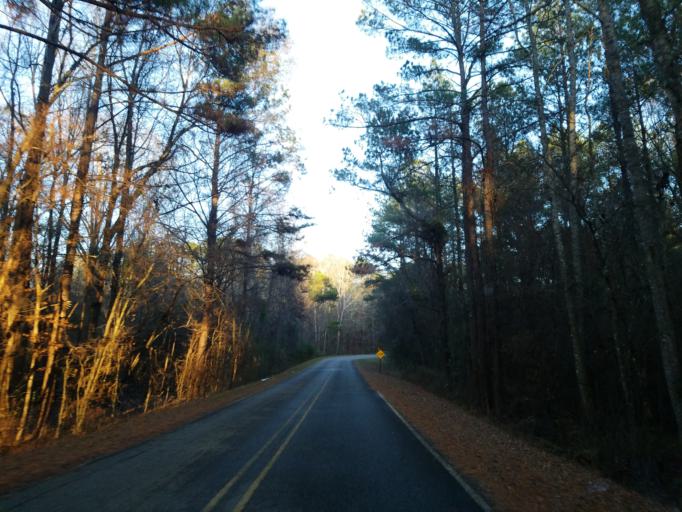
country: US
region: Mississippi
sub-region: Lauderdale County
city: Meridian
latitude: 32.2671
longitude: -88.7896
